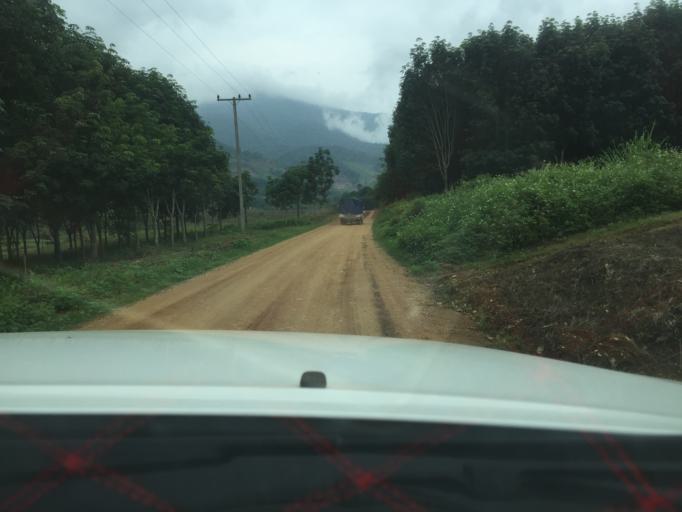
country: TH
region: Phayao
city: Phu Sang
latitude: 19.7415
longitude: 100.4477
